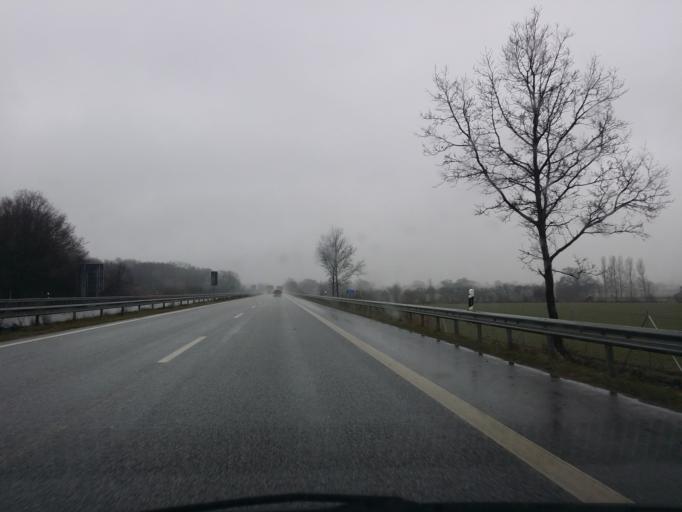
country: DE
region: Schleswig-Holstein
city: Kabelhorst
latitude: 54.2126
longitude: 10.9015
